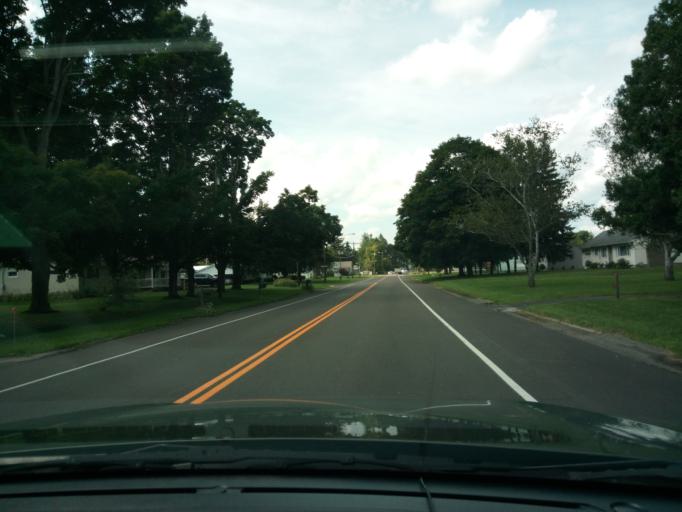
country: US
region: New York
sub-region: Chemung County
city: Southport
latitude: 42.0549
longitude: -76.7809
